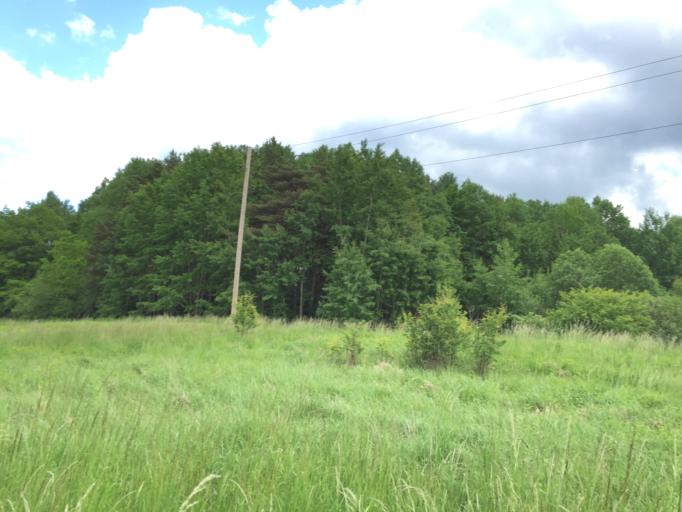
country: LV
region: Dobeles Rajons
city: Dobele
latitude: 56.6577
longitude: 23.2946
